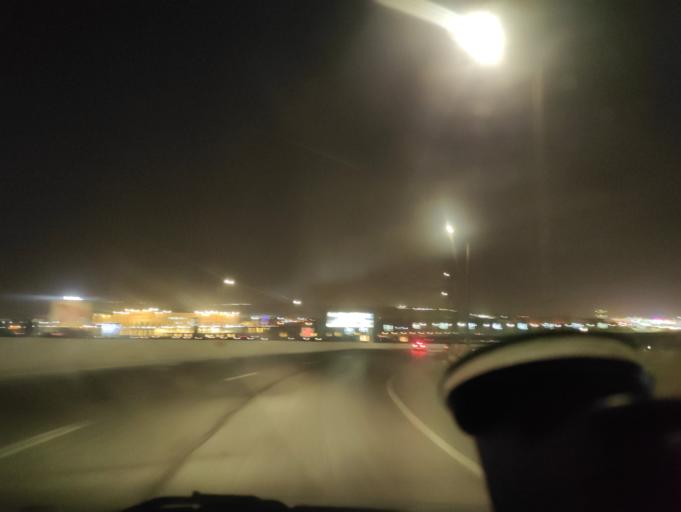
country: EG
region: Al Jizah
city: Awsim
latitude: 30.0468
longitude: 31.0551
